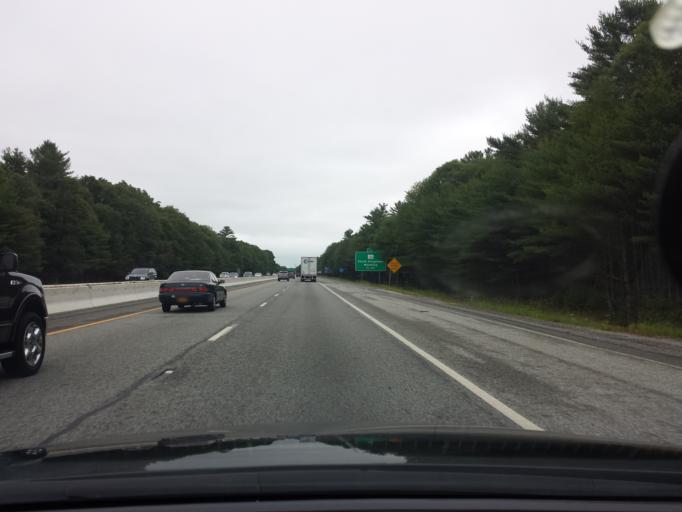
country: US
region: Rhode Island
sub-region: Washington County
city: Hope Valley
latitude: 41.5048
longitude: -71.7012
